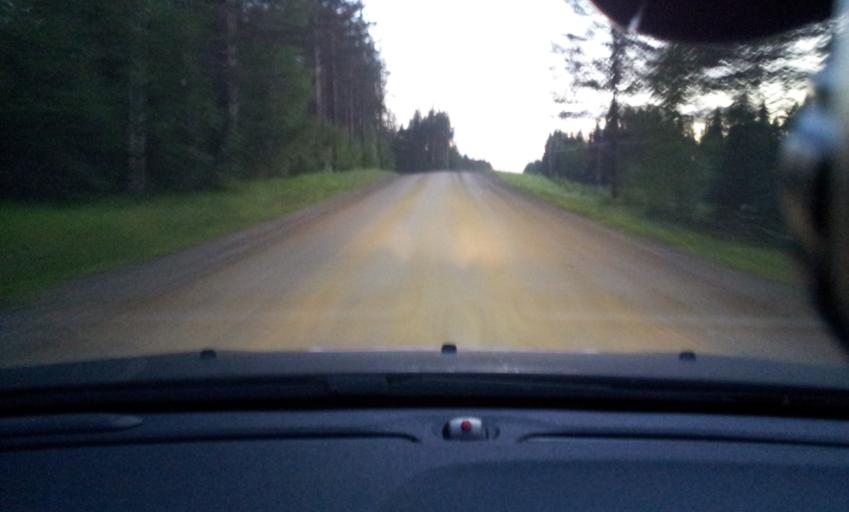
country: SE
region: Jaemtland
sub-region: Braecke Kommun
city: Braecke
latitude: 62.7255
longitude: 15.5072
